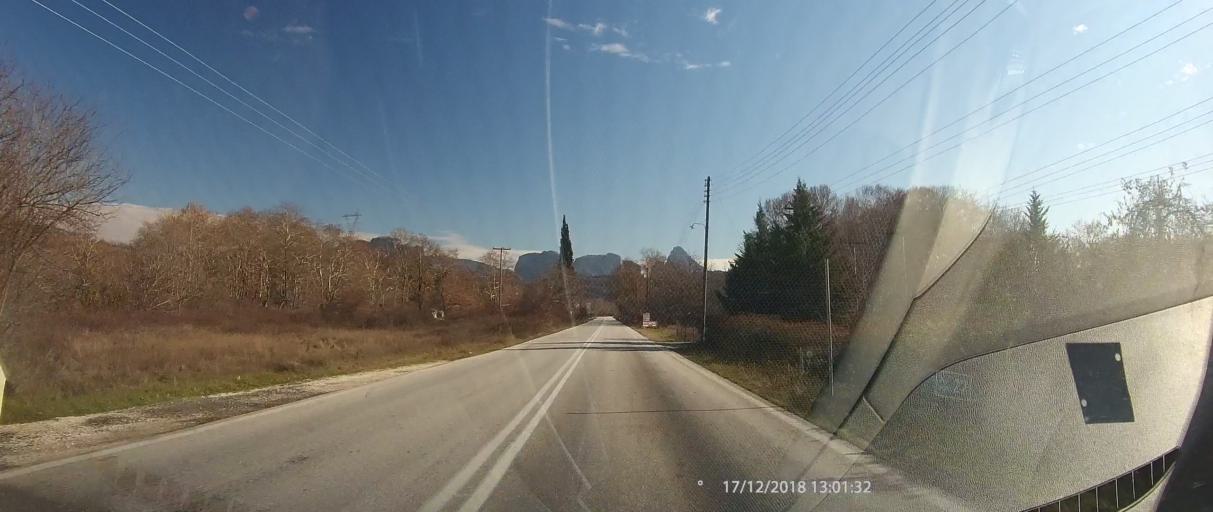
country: GR
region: Thessaly
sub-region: Trikala
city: Kastraki
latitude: 39.7320
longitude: 21.5843
